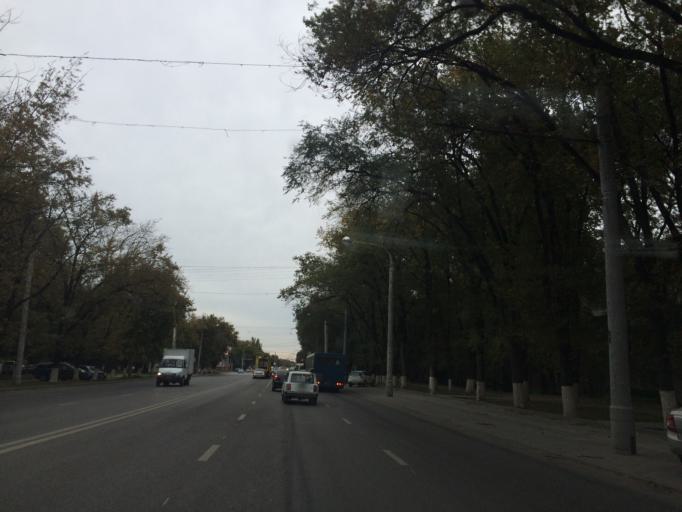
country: RU
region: Rostov
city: Rostov-na-Donu
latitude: 47.2122
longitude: 39.6426
